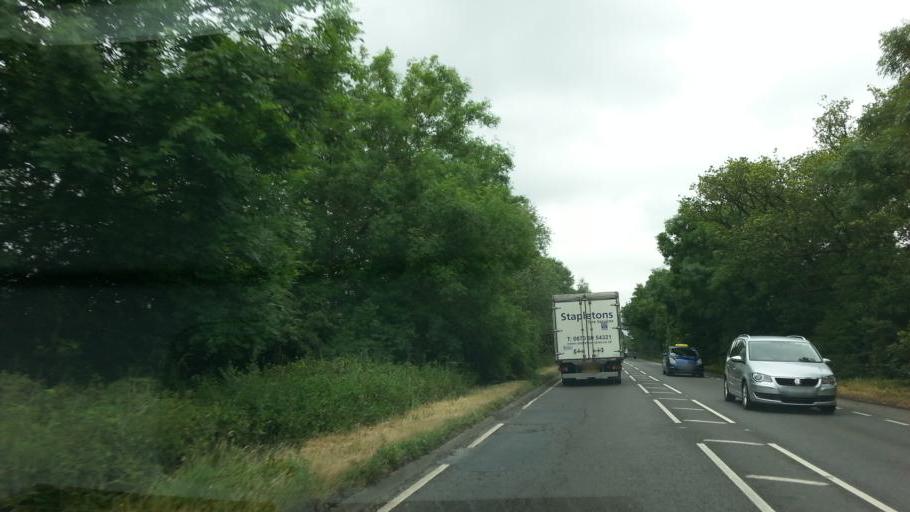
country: GB
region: England
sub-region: Northamptonshire
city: Broughton
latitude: 52.3206
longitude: -0.7992
